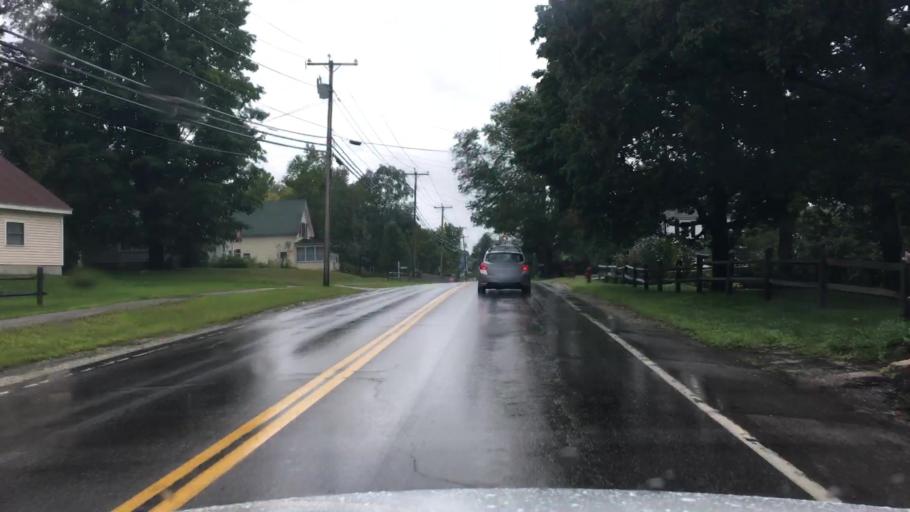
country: US
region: New Hampshire
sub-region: Carroll County
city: Conway
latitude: 43.9795
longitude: -71.1104
